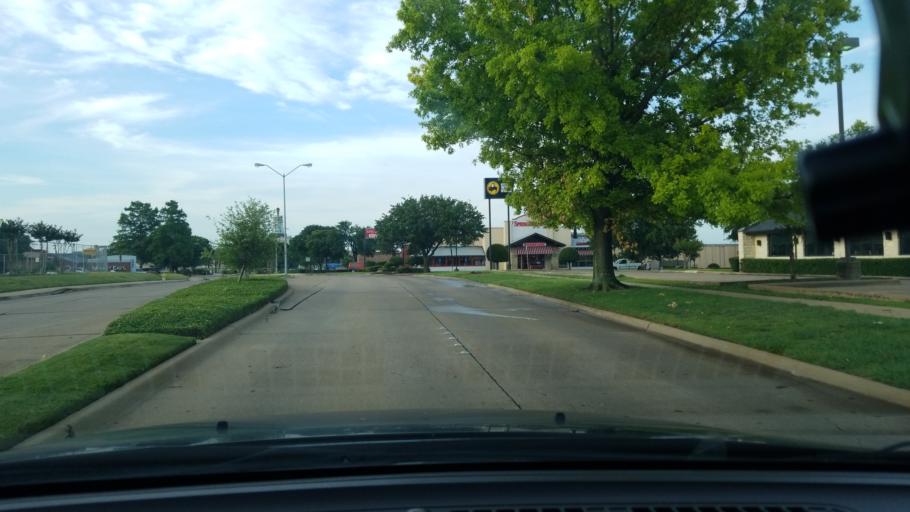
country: US
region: Texas
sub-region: Dallas County
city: Mesquite
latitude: 32.8129
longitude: -96.6258
